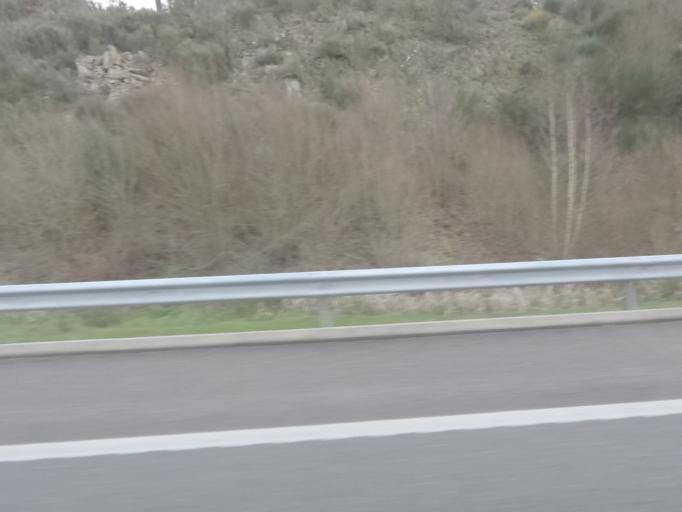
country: ES
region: Galicia
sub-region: Provincia de Ourense
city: Punxin
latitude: 42.3677
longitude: -7.9947
